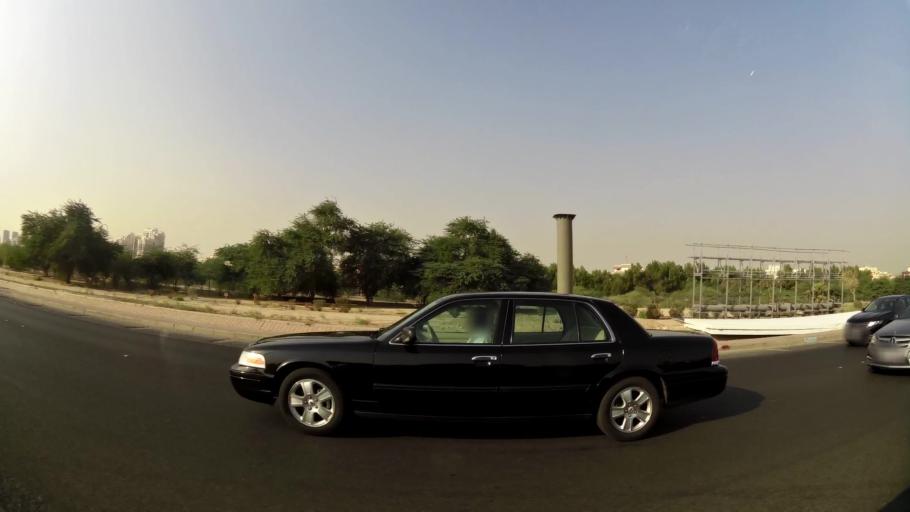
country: KW
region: Muhafazat Hawalli
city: Salwa
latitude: 29.2742
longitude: 48.0820
